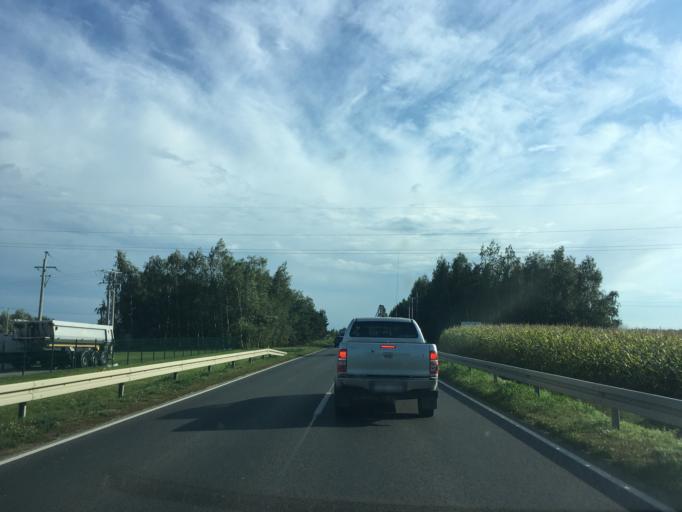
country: PL
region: Kujawsko-Pomorskie
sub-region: Powiat wabrzeski
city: Wabrzezno
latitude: 53.2700
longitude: 18.9375
